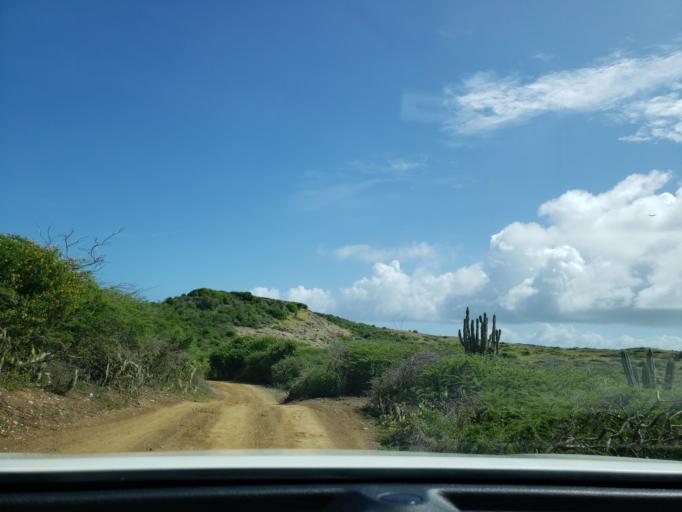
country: CW
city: Barber
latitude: 12.3639
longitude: -69.1146
